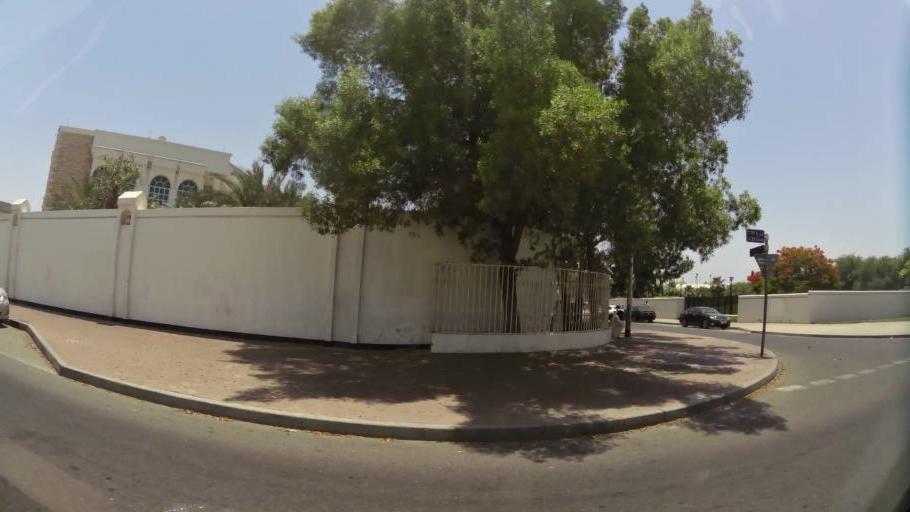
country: AE
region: Ash Shariqah
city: Sharjah
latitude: 25.2847
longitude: 55.3335
